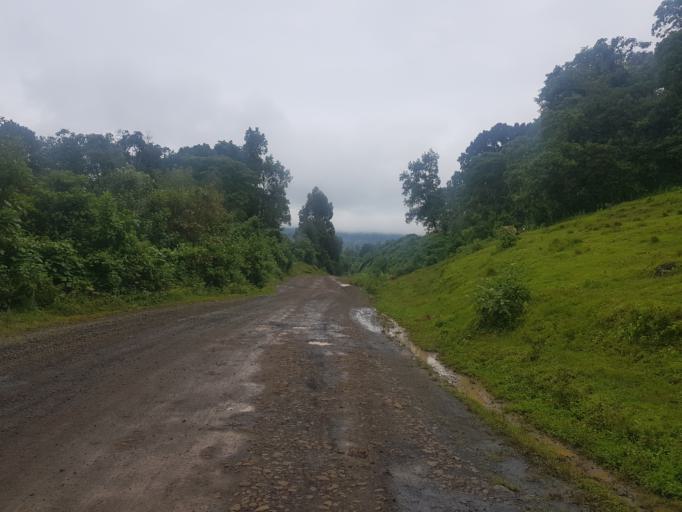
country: ET
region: Southern Nations, Nationalities, and People's Region
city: Tippi
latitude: 7.6697
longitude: 35.5014
